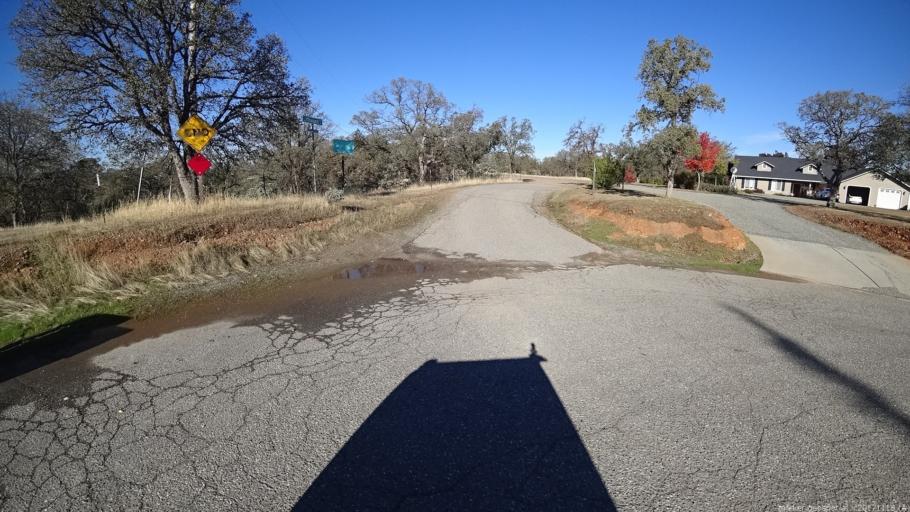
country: US
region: California
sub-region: Shasta County
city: Cottonwood
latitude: 40.3985
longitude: -122.3261
